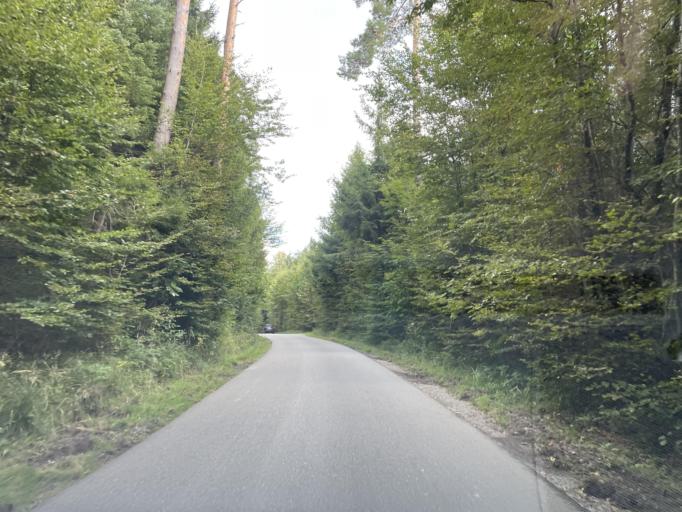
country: CH
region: Zurich
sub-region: Bezirk Winterthur
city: Stadt Winterthur (Kreis 1) / Heiligberg
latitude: 47.4781
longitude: 8.7295
